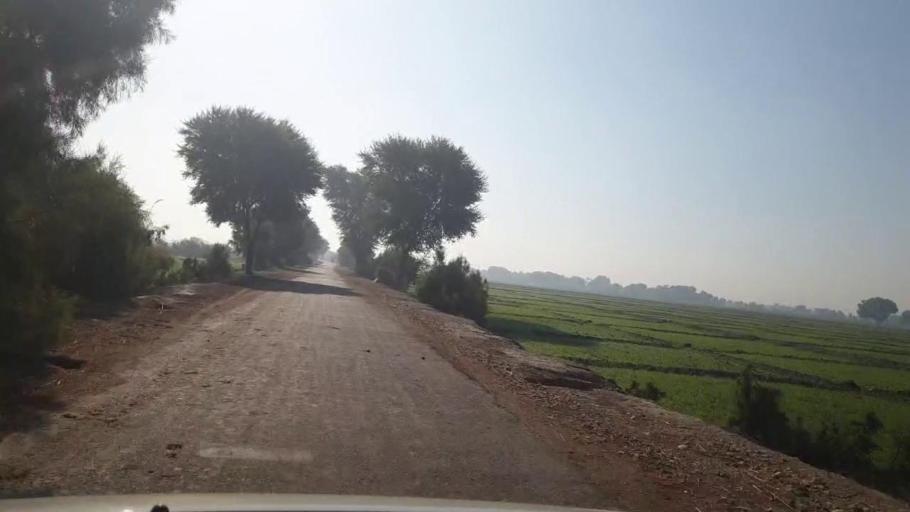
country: PK
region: Sindh
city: Dadu
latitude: 26.6623
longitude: 67.8189
